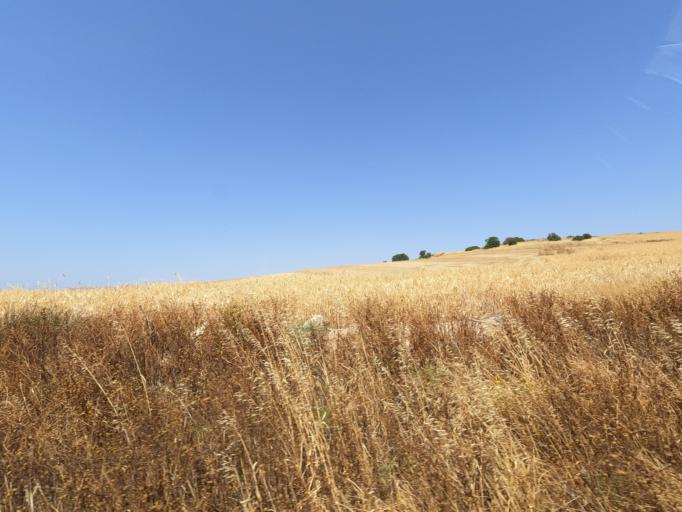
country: CY
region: Larnaka
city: Troulloi
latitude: 35.0368
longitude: 33.6242
